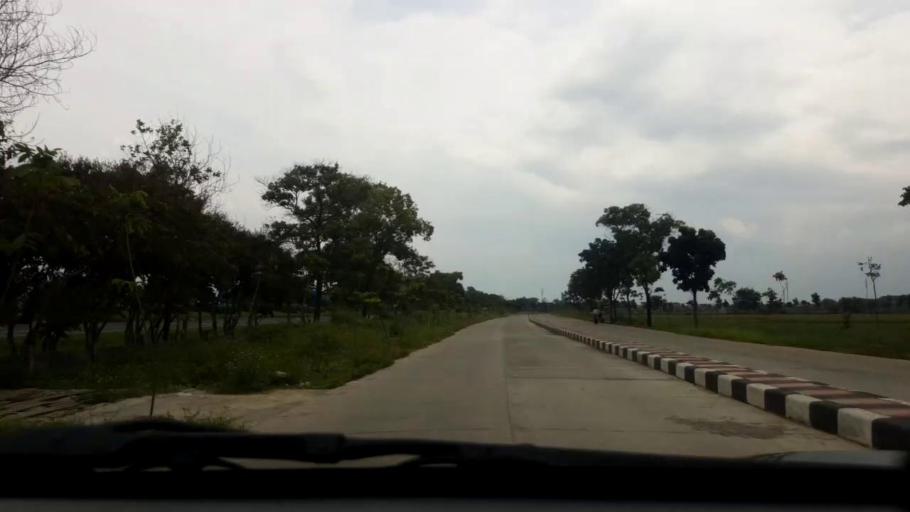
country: ID
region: West Java
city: Cileunyi
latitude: -6.9632
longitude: 107.7123
